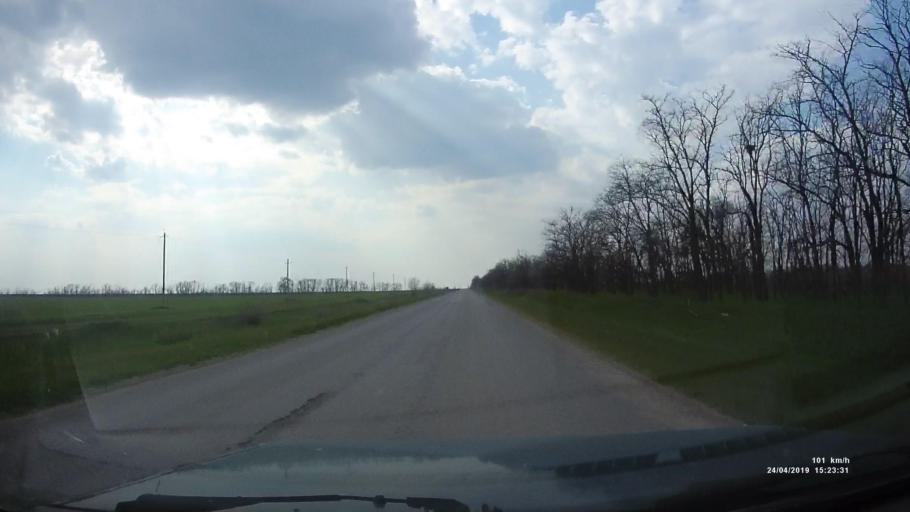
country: RU
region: Rostov
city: Remontnoye
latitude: 46.5436
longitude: 43.0883
